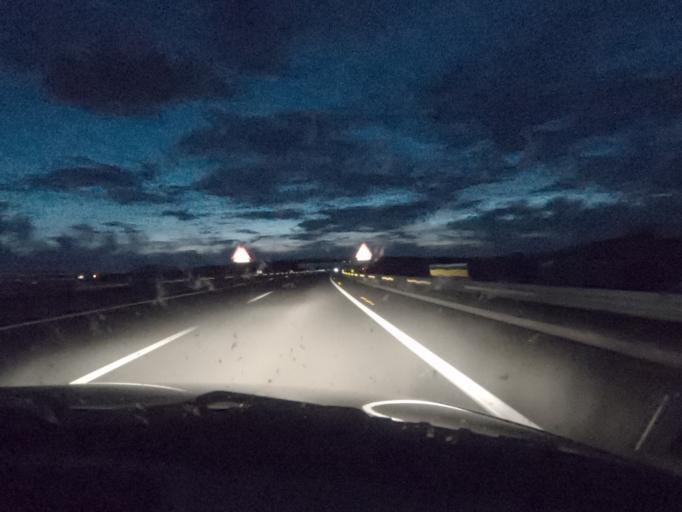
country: ES
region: Extremadura
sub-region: Provincia de Caceres
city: Morcillo
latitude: 39.9747
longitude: -6.3632
